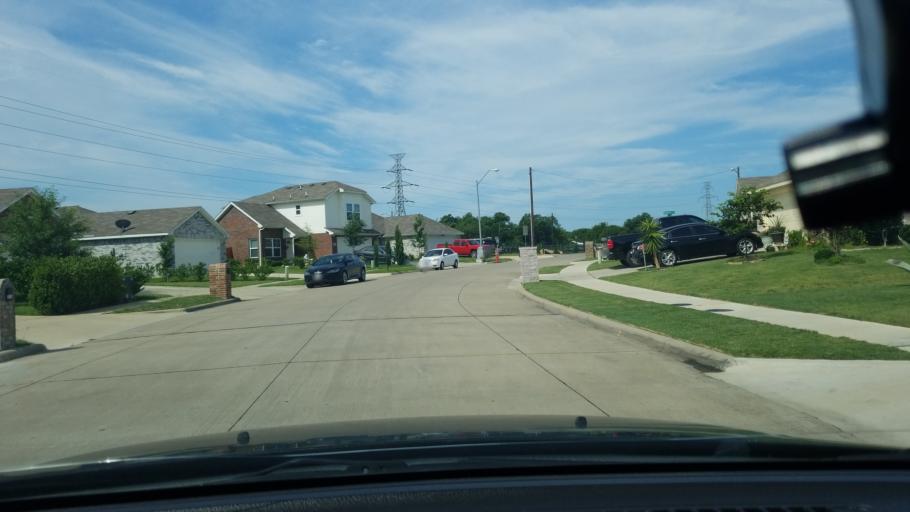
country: US
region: Texas
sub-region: Dallas County
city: Balch Springs
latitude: 32.7697
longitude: -96.6741
